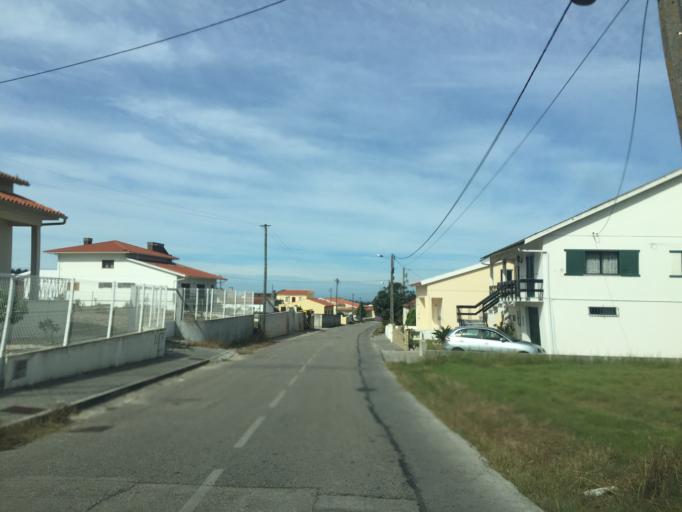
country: PT
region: Coimbra
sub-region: Figueira da Foz
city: Lavos
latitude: 40.0807
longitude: -8.8291
